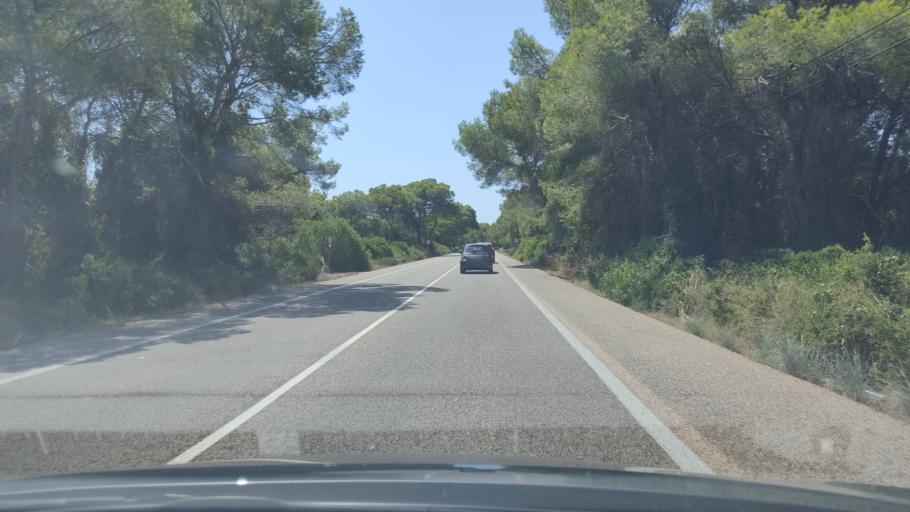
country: ES
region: Valencia
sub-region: Provincia de Valencia
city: Sollana
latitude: 39.3278
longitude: -0.3116
